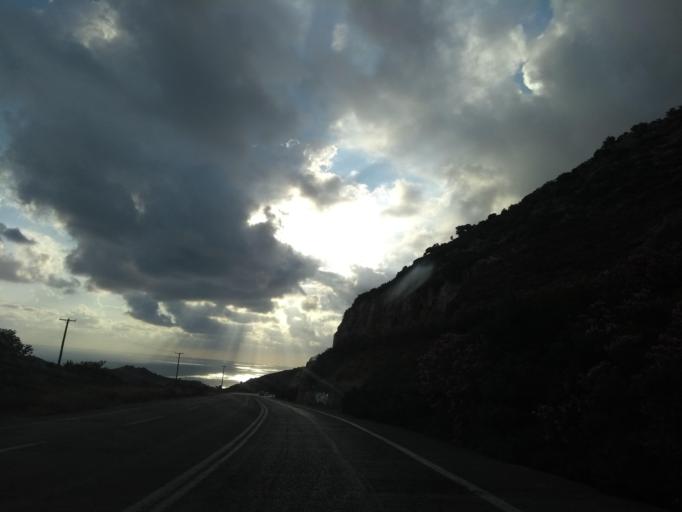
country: GR
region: Crete
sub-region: Nomos Rethymnis
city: Perama
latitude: 35.4071
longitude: 24.7588
